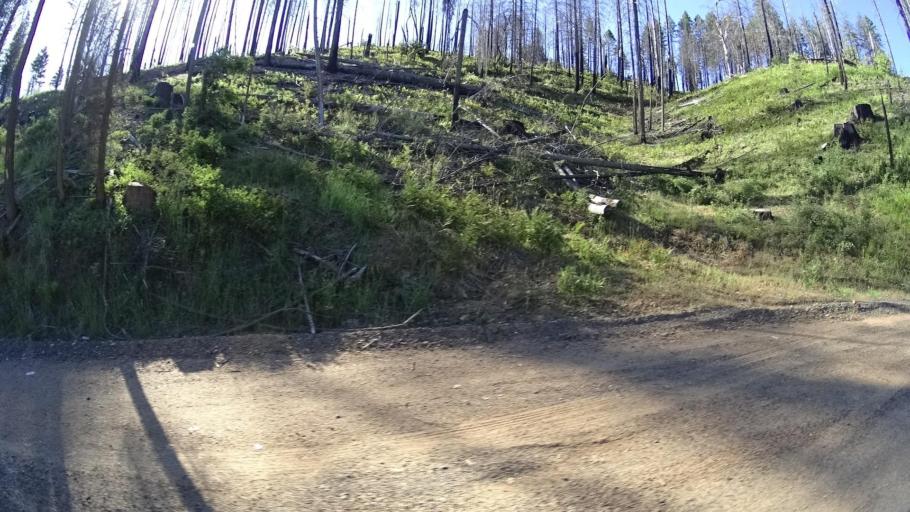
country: US
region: California
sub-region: Lake County
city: Upper Lake
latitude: 39.3794
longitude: -122.9884
